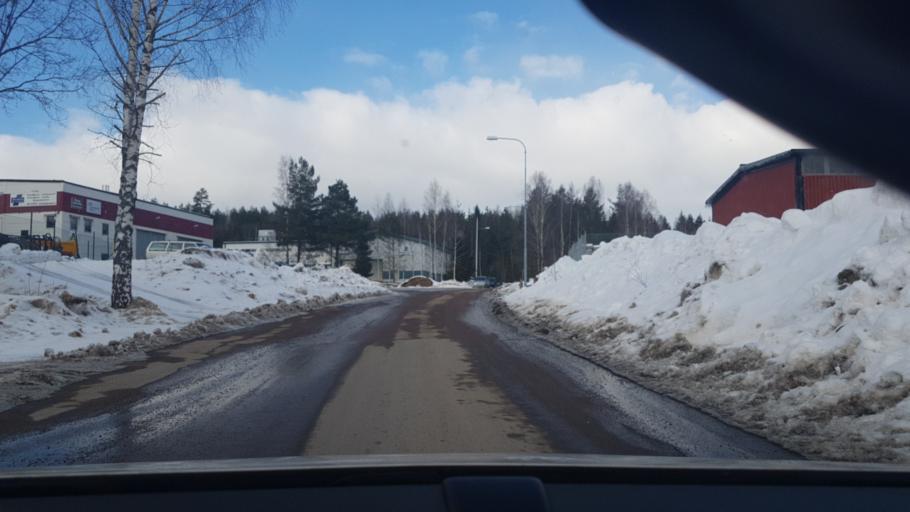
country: SE
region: Vaermland
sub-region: Arvika Kommun
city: Arvika
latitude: 59.6676
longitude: 12.6299
